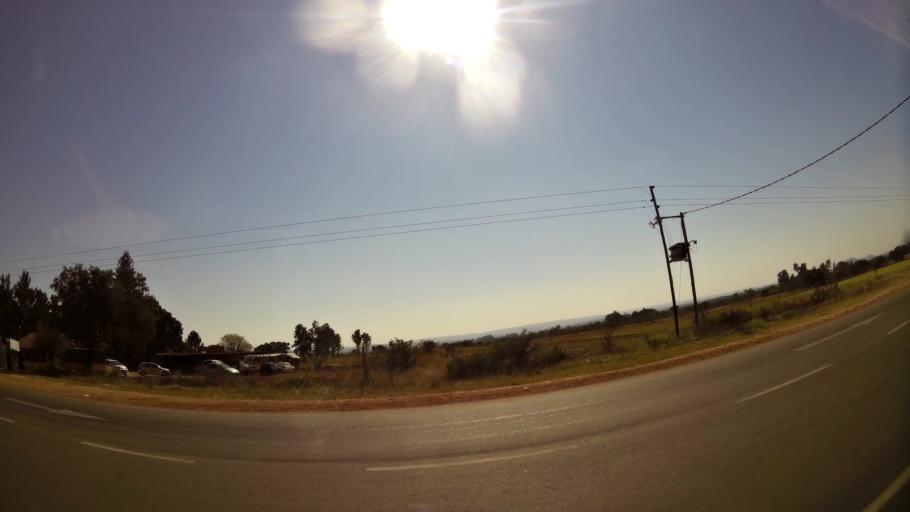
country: ZA
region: North-West
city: Ga-Rankuwa
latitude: -25.6608
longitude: 28.0467
